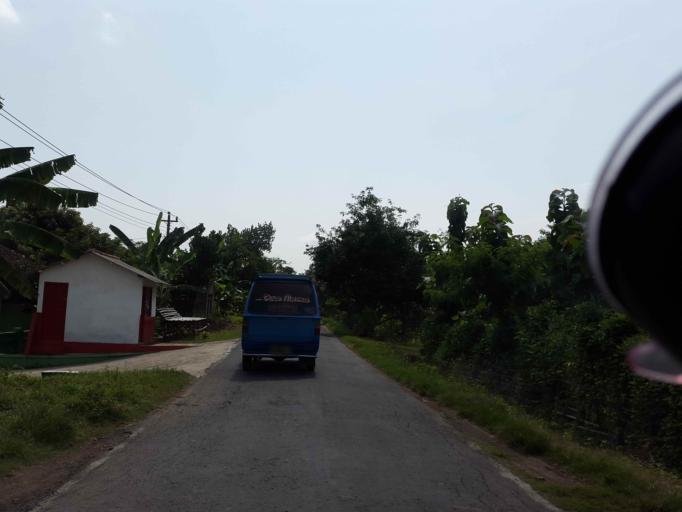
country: ID
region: Central Java
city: Pemalang
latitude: -6.9499
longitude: 109.3669
